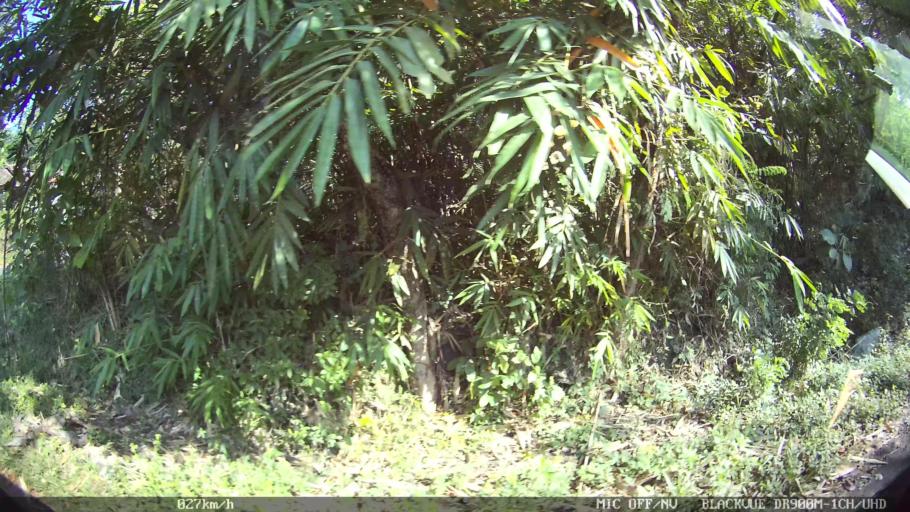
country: ID
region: Daerah Istimewa Yogyakarta
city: Kasihan
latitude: -7.8247
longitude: 110.2908
